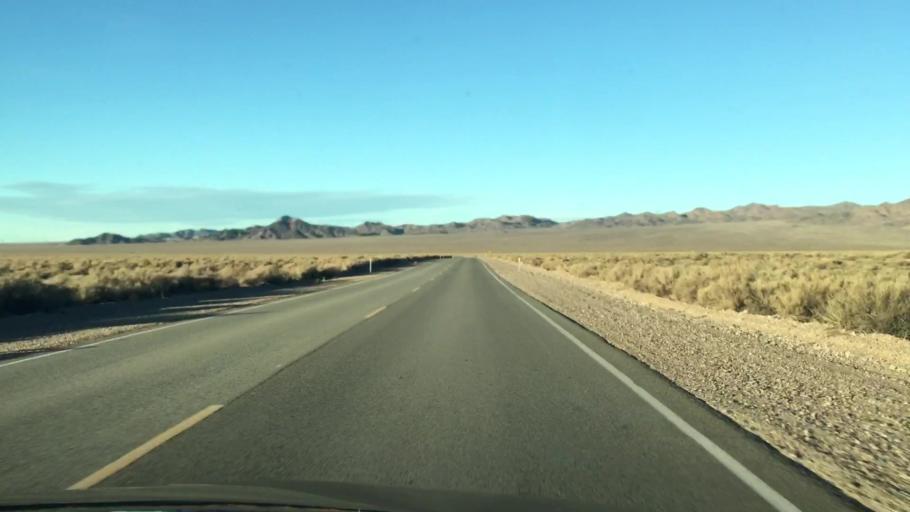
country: US
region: California
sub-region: San Bernardino County
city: Fort Irwin
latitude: 35.3226
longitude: -116.0820
